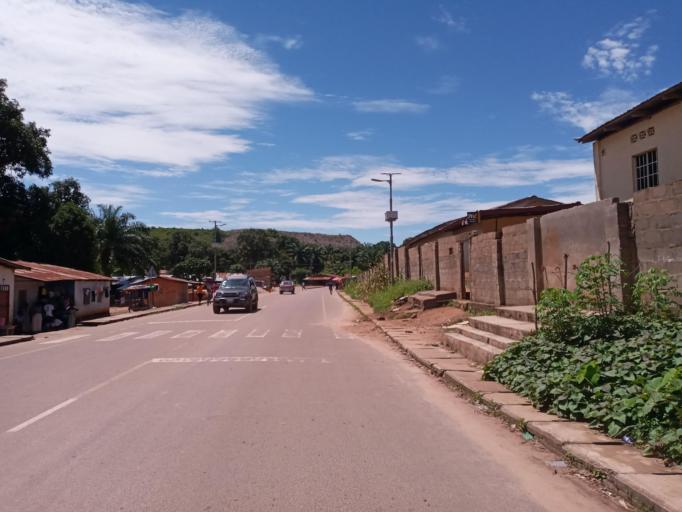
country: SL
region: Eastern Province
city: Koidu
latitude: 8.6398
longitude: -10.9700
